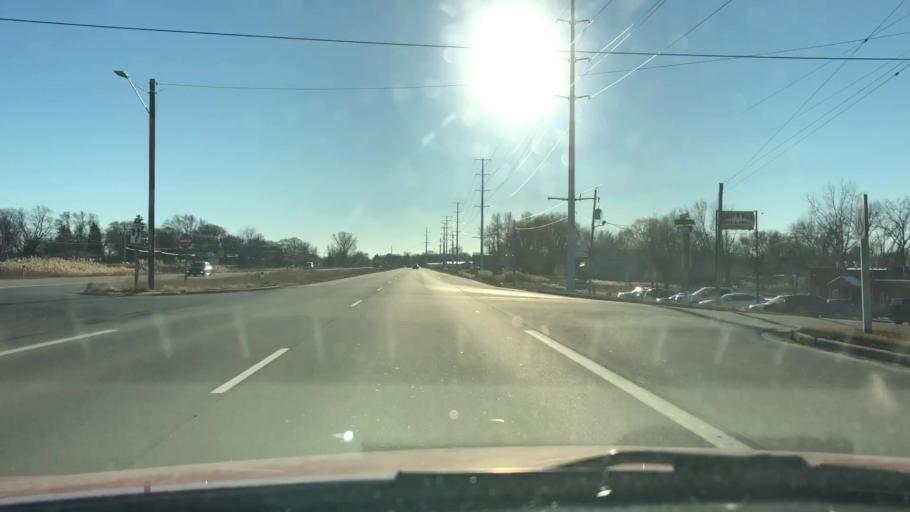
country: US
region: Wisconsin
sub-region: Brown County
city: De Pere
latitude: 44.4623
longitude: -88.0724
